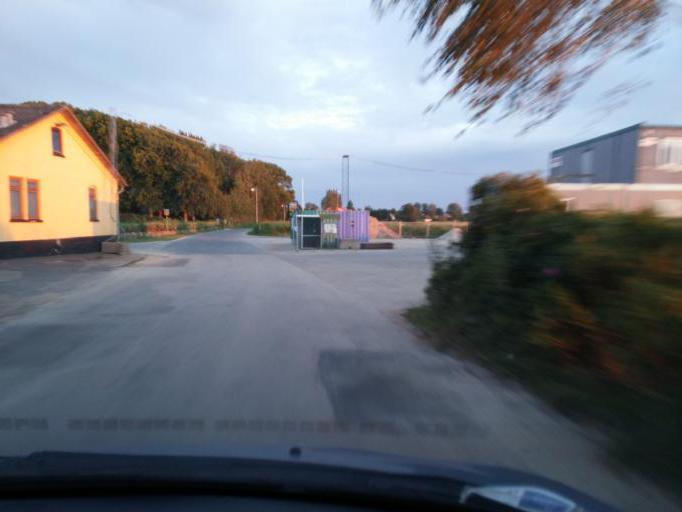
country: DK
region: South Denmark
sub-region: Kerteminde Kommune
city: Munkebo
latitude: 55.4283
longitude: 10.5837
